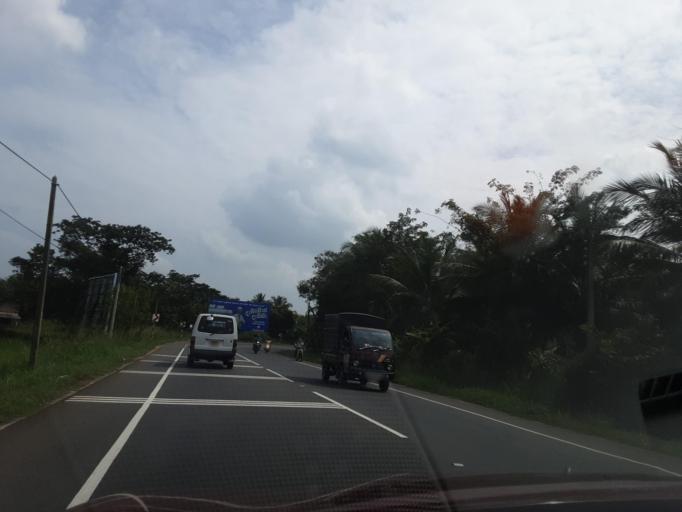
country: LK
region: North Central
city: Anuradhapura
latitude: 8.4784
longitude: 80.5120
